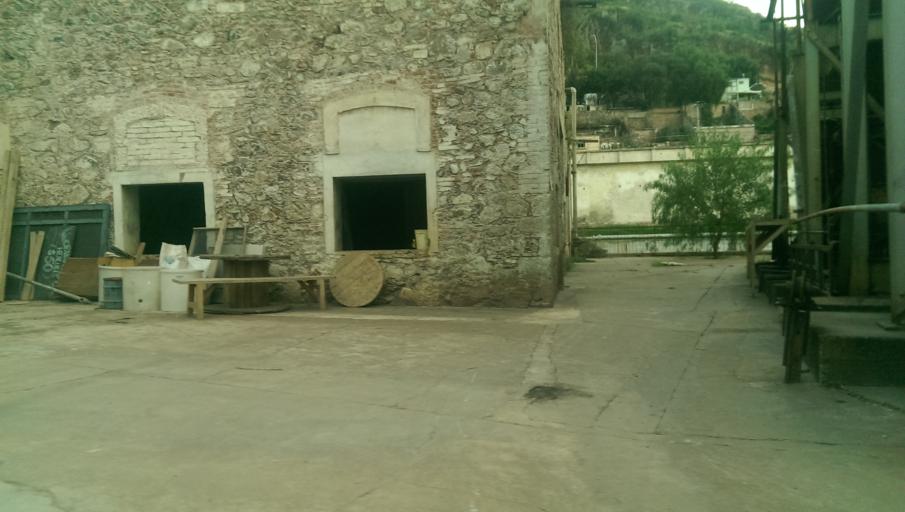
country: MX
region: Queretaro
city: La Canada
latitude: 20.6001
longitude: -100.3547
